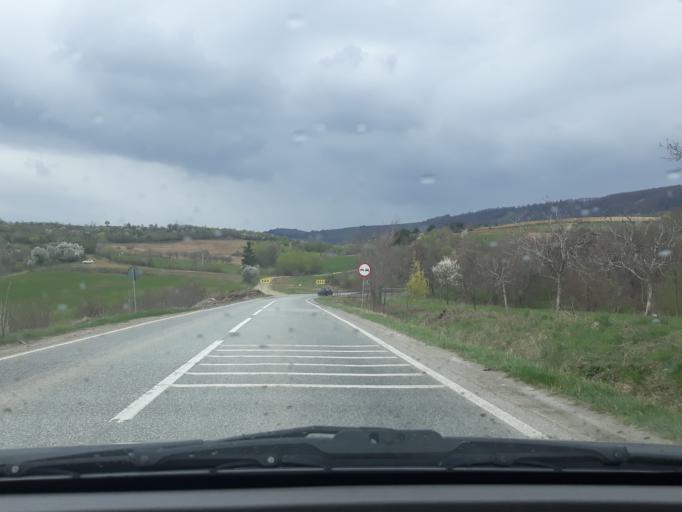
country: RO
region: Harghita
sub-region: Comuna Lupeni
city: Lupeni
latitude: 46.3951
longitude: 25.2131
